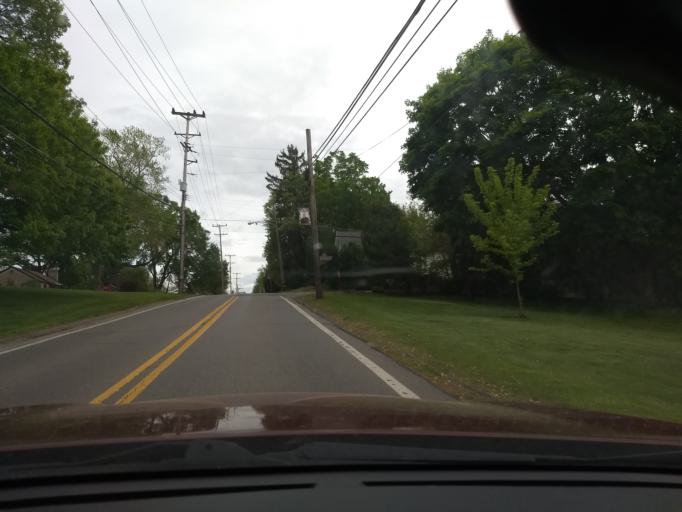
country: US
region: Pennsylvania
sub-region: Allegheny County
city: Coraopolis
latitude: 40.4836
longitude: -80.1365
